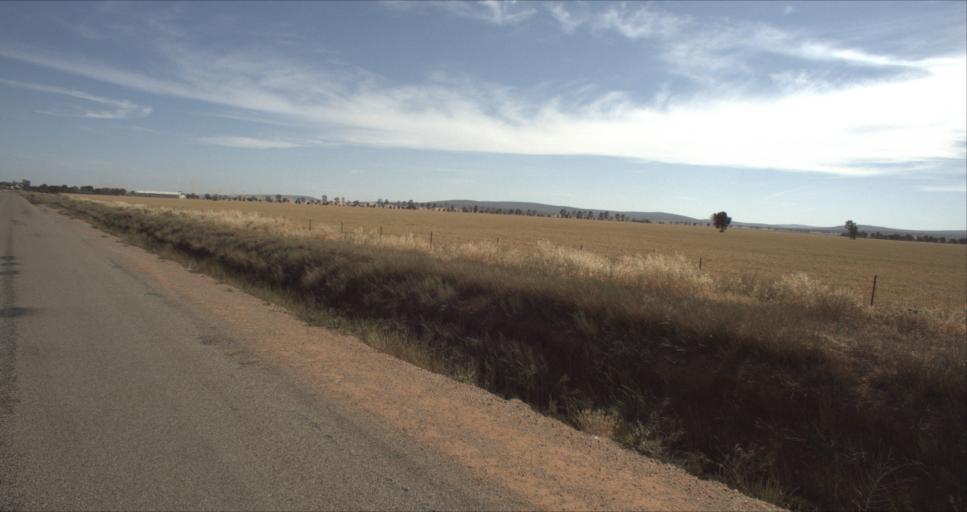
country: AU
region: New South Wales
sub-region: Leeton
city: Leeton
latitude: -34.5700
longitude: 146.4737
